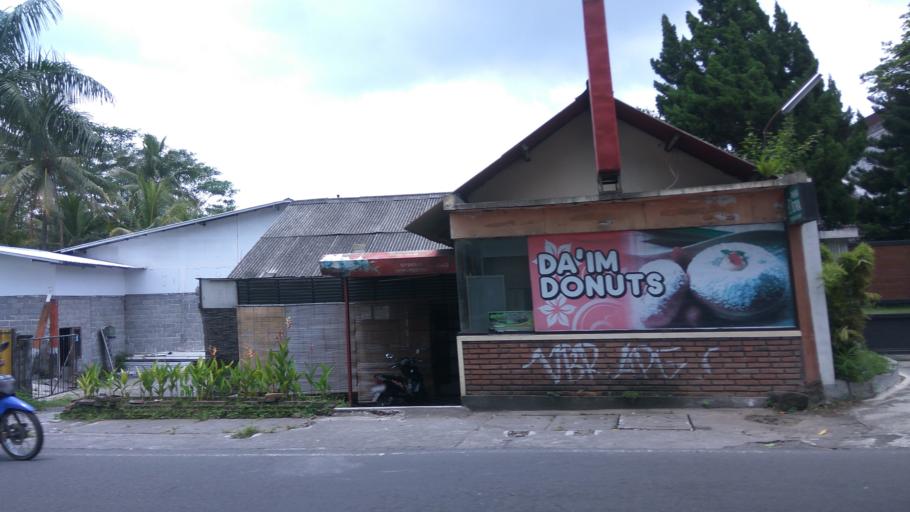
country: ID
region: Daerah Istimewa Yogyakarta
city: Melati
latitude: -7.7230
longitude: 110.4020
